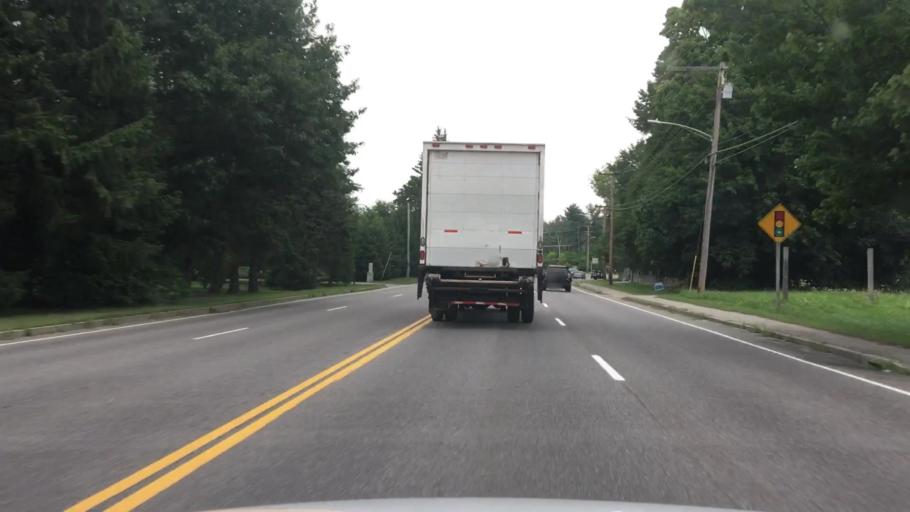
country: US
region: Maine
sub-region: Cumberland County
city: South Portland Gardens
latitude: 43.6496
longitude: -70.3247
